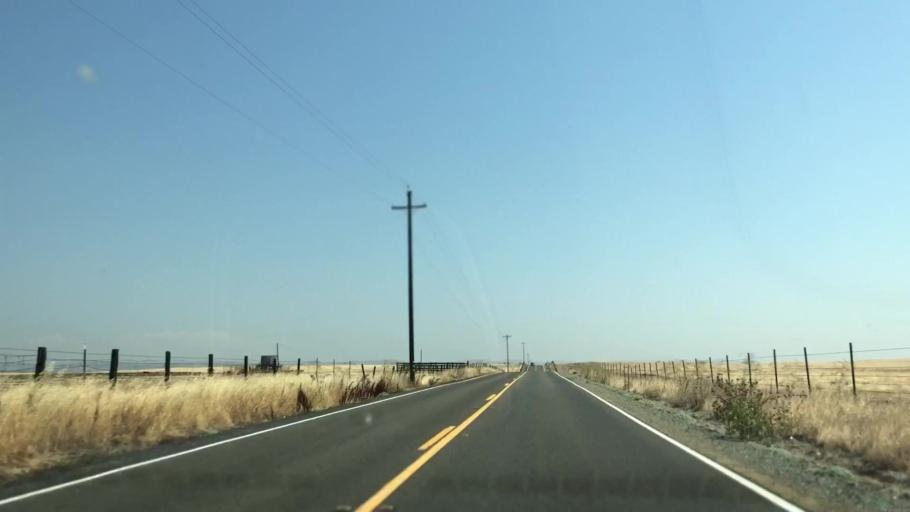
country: US
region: California
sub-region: San Joaquin County
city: Escalon
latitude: 37.9449
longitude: -120.9227
